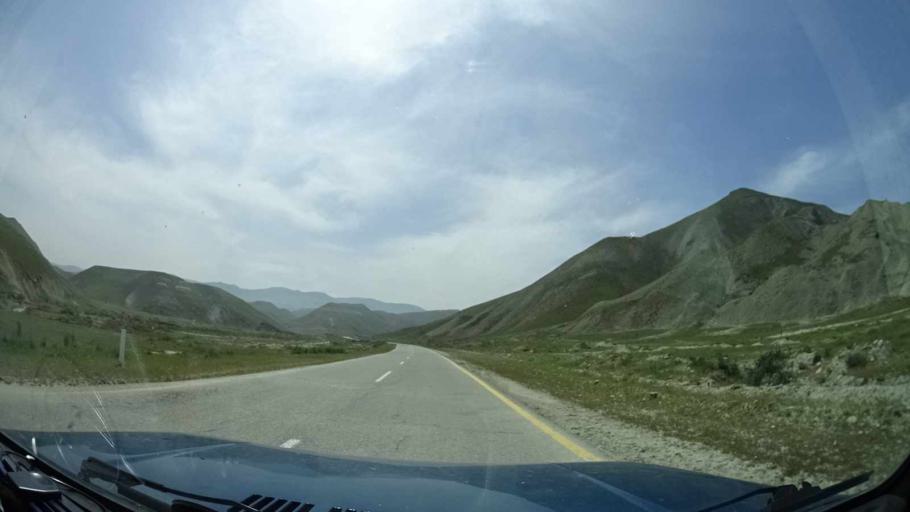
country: AZ
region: Xizi
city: Kilyazi
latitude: 40.8550
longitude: 49.2755
